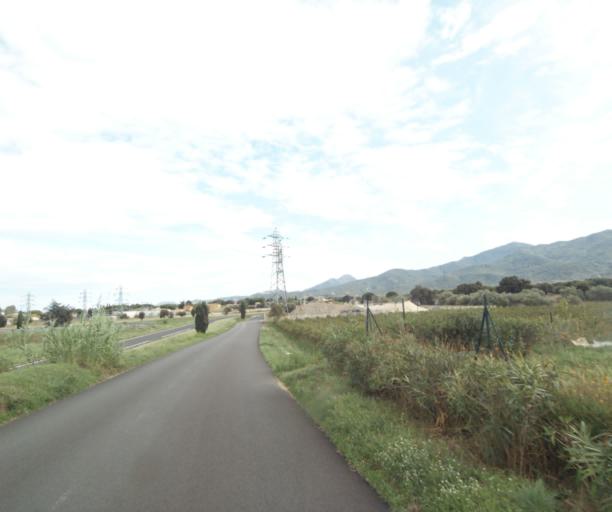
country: FR
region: Languedoc-Roussillon
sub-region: Departement des Pyrenees-Orientales
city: Argelers
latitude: 42.5502
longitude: 3.0039
